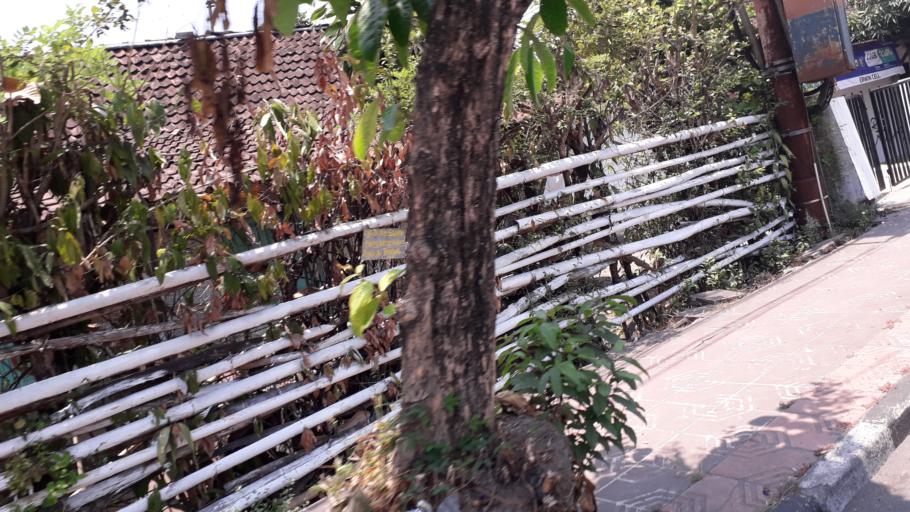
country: ID
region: Daerah Istimewa Yogyakarta
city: Yogyakarta
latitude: -7.7637
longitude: 110.3693
